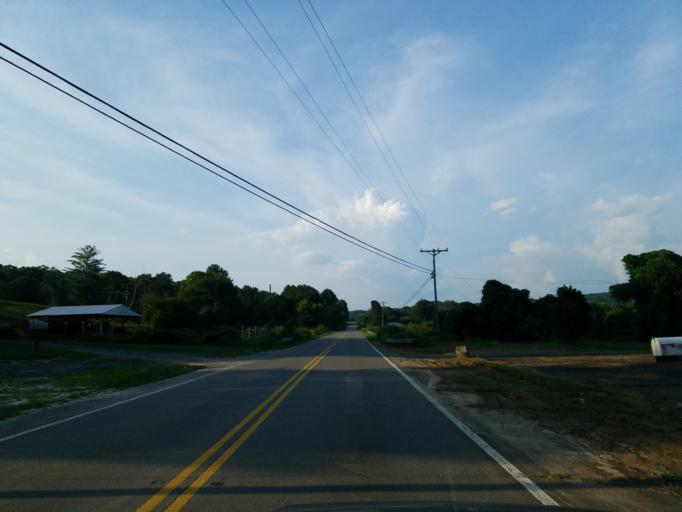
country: US
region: Georgia
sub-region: Pickens County
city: Jasper
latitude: 34.5612
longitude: -84.5386
